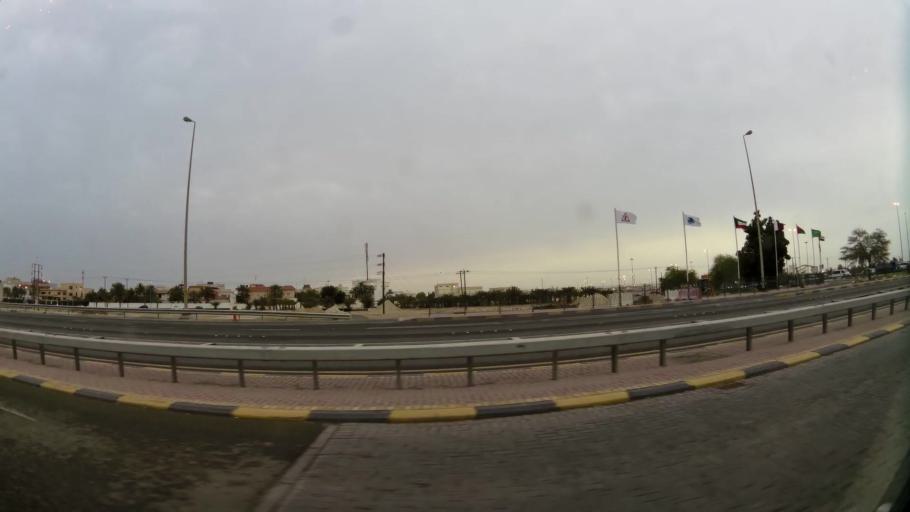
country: BH
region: Northern
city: Madinat `Isa
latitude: 26.1565
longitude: 50.5363
